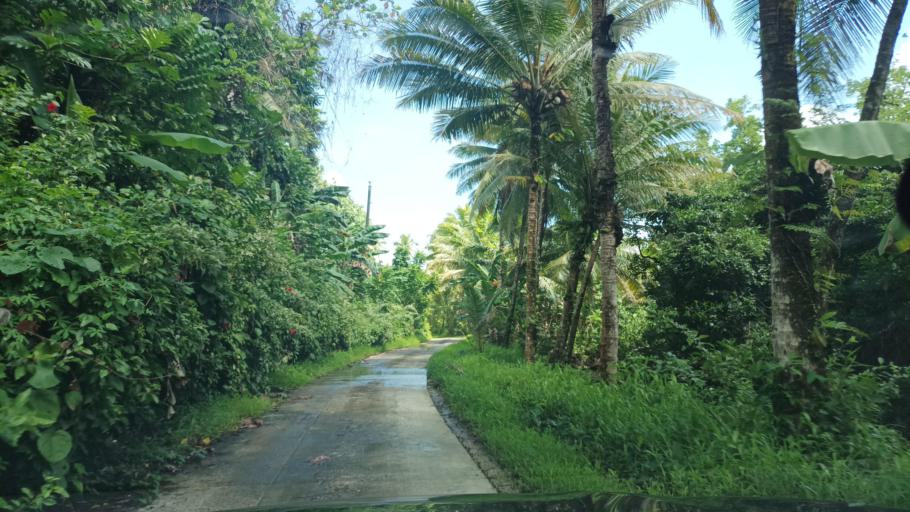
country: FM
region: Pohnpei
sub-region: Sokehs Municipality
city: Palikir - National Government Center
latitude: 6.9406
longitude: 158.1662
